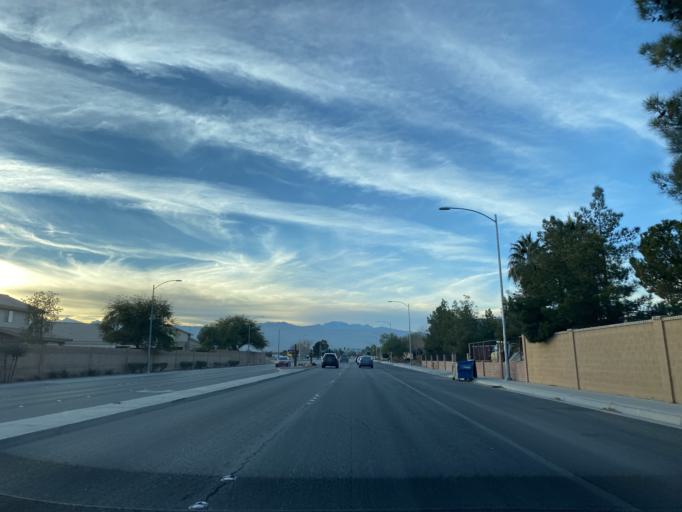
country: US
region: Nevada
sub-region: Clark County
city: Las Vegas
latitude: 36.2617
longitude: -115.2300
